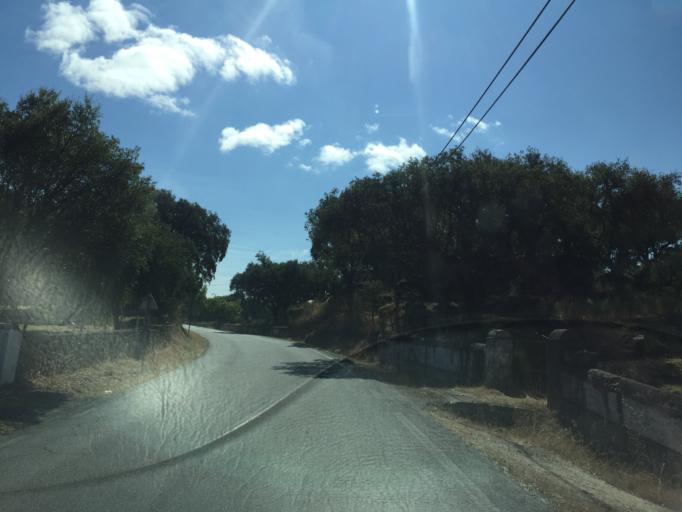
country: PT
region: Portalegre
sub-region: Marvao
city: Marvao
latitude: 39.4332
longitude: -7.3625
